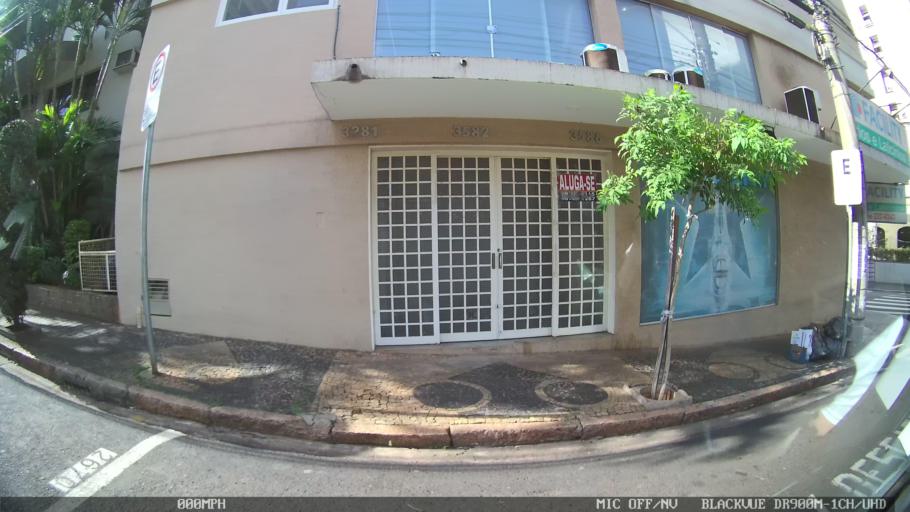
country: BR
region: Sao Paulo
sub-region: Sao Jose Do Rio Preto
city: Sao Jose do Rio Preto
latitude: -20.8171
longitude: -49.3830
